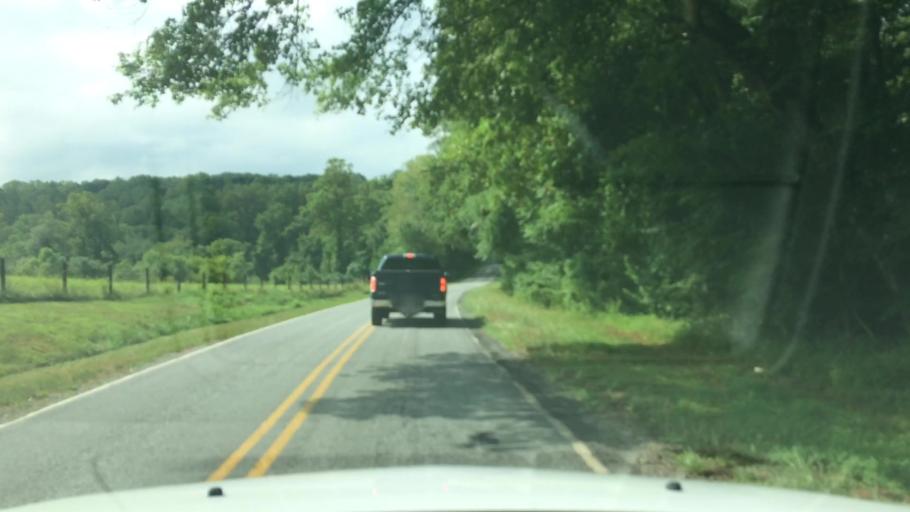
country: US
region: North Carolina
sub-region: Yadkin County
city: Jonesville
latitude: 36.1102
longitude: -80.8565
